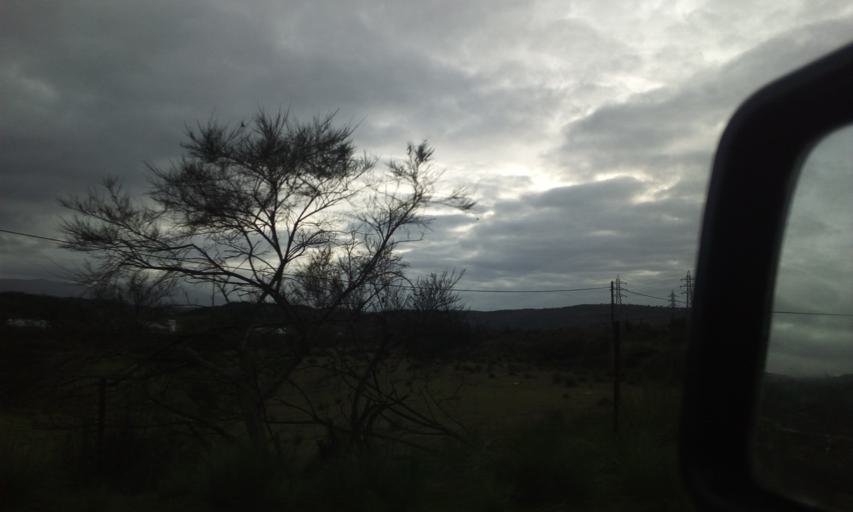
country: PT
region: Guarda
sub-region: Celorico da Beira
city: Celorico da Beira
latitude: 40.6327
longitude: -7.4139
